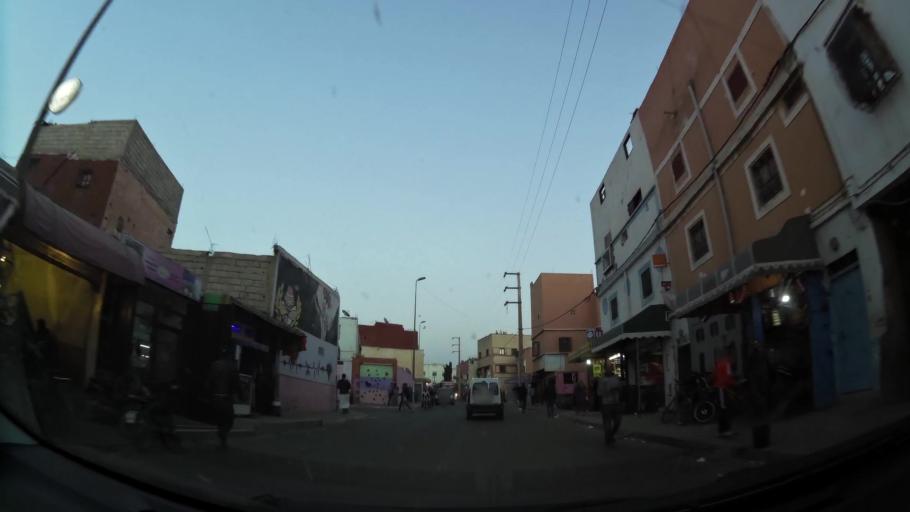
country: MA
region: Souss-Massa-Draa
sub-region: Inezgane-Ait Mellou
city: Inezgane
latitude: 30.3753
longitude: -9.4938
